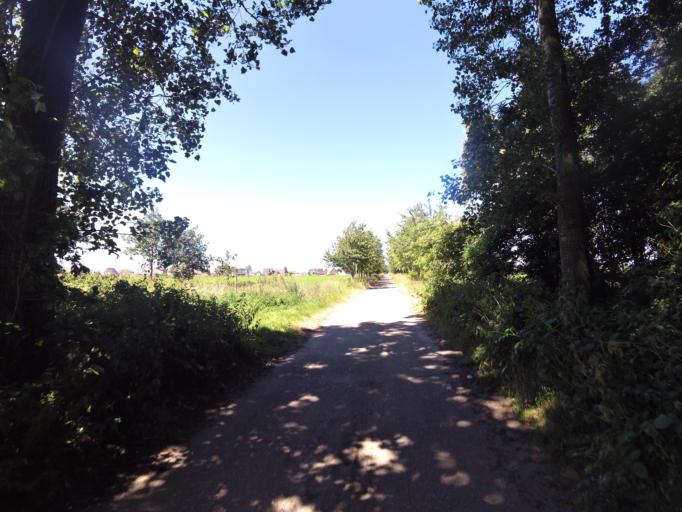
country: BE
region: Flanders
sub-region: Provincie West-Vlaanderen
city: Ichtegem
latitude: 51.0804
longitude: 3.0442
